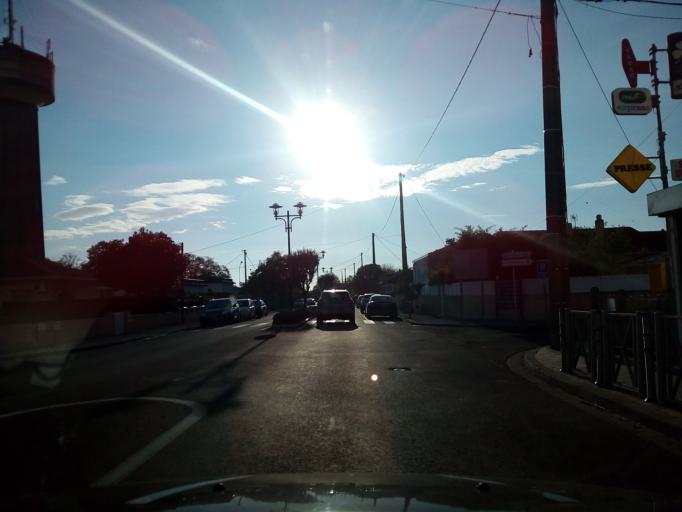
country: FR
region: Aquitaine
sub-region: Departement de la Gironde
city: Andernos-les-Bains
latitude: 44.7453
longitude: -1.0937
